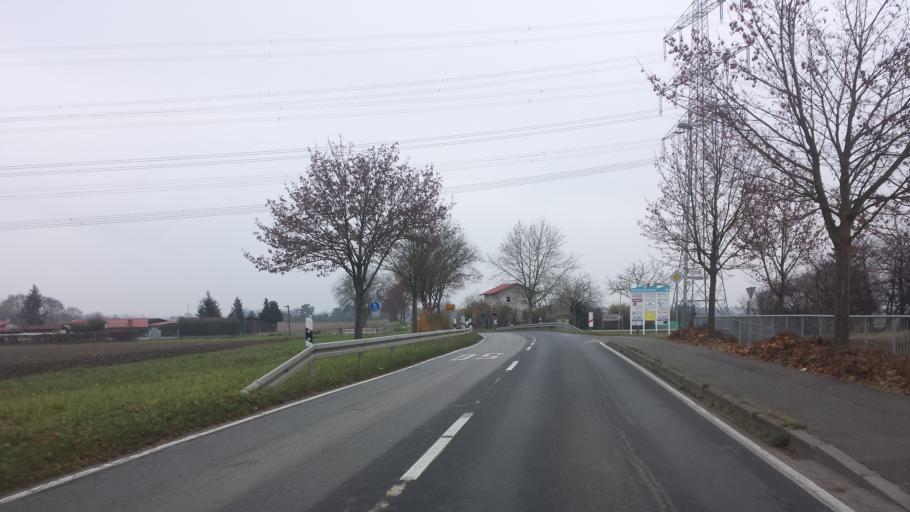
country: DE
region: Hesse
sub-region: Regierungsbezirk Darmstadt
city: Burstadt
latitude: 49.6592
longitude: 8.4264
